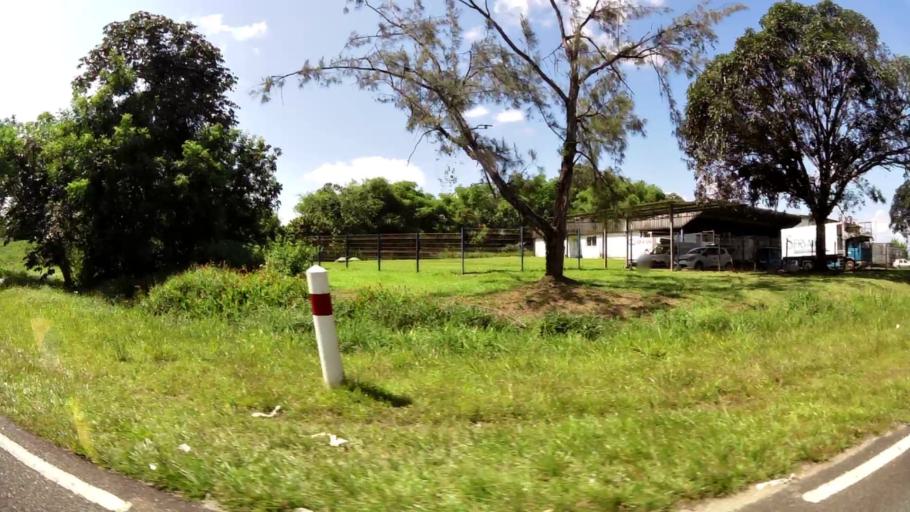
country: GF
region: Guyane
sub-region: Guyane
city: Matoury
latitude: 4.8274
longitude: -52.3592
